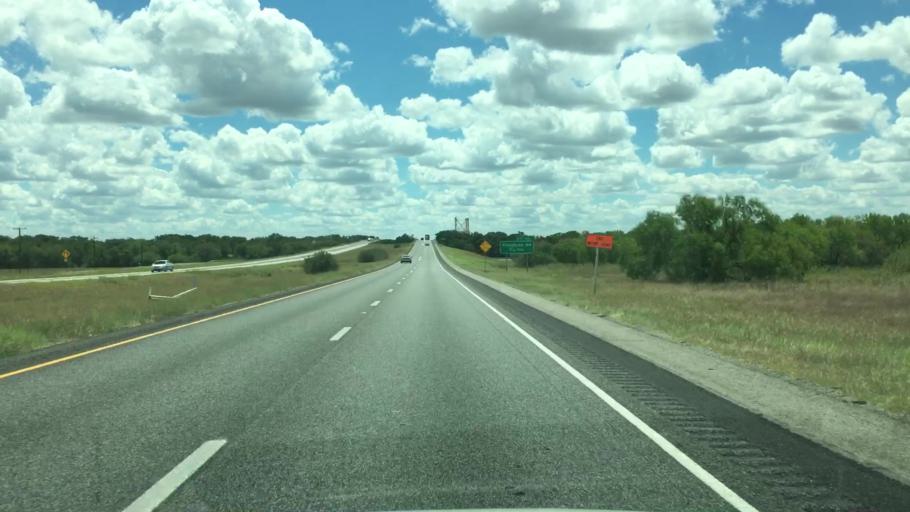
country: US
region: Texas
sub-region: Atascosa County
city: Pleasanton
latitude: 28.9672
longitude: -98.4363
